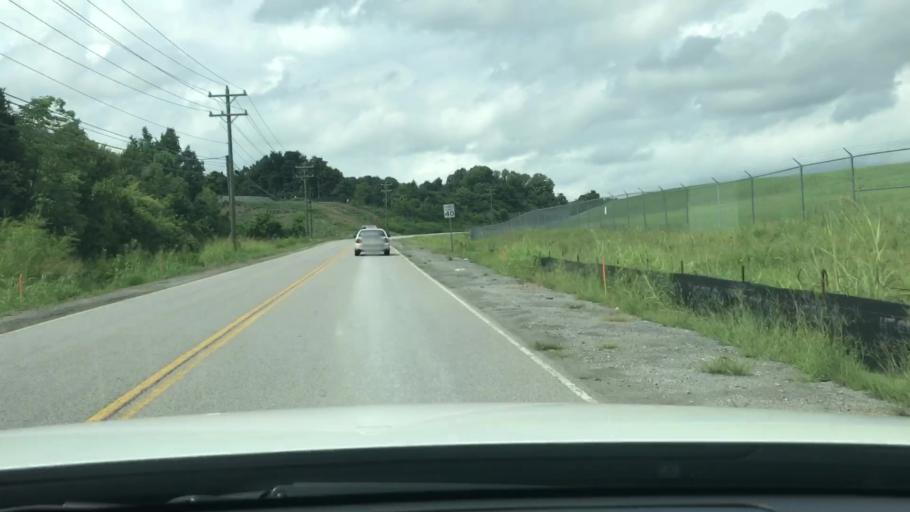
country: US
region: Tennessee
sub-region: Davidson County
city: Oak Hill
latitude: 36.0973
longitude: -86.6917
